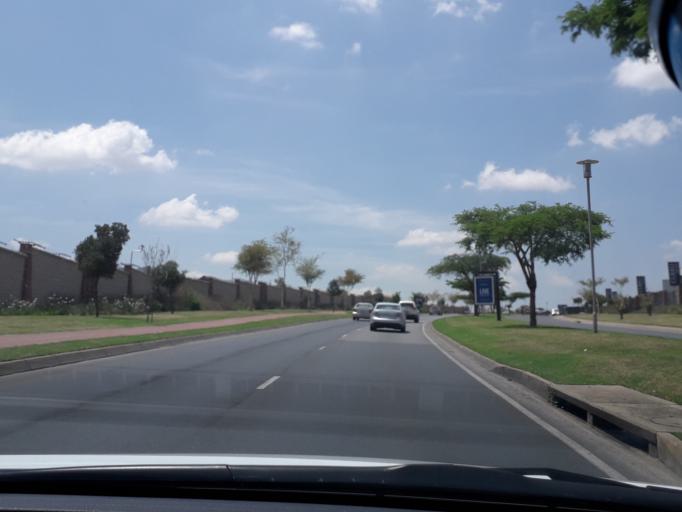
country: ZA
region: Gauteng
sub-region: City of Johannesburg Metropolitan Municipality
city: Midrand
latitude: -26.0156
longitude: 28.0933
